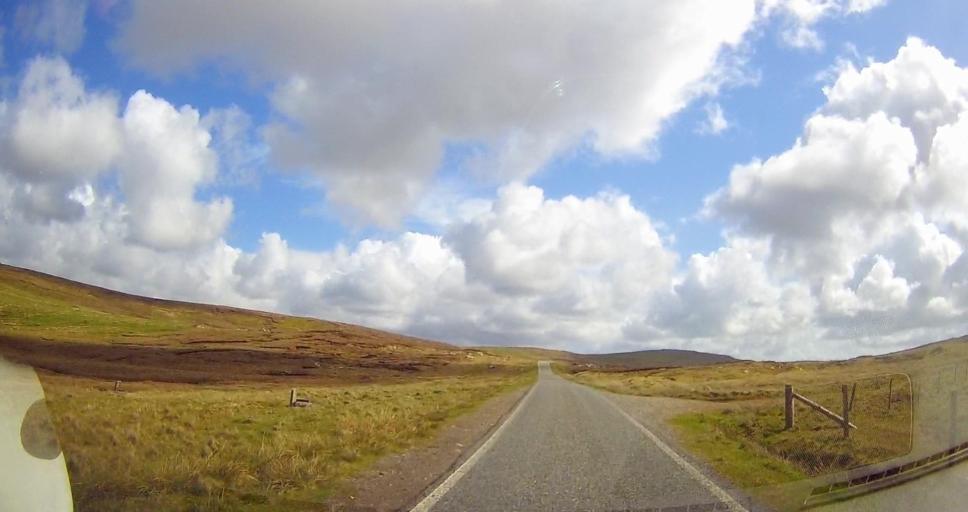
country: GB
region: Scotland
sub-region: Shetland Islands
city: Lerwick
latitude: 60.4996
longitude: -1.3980
